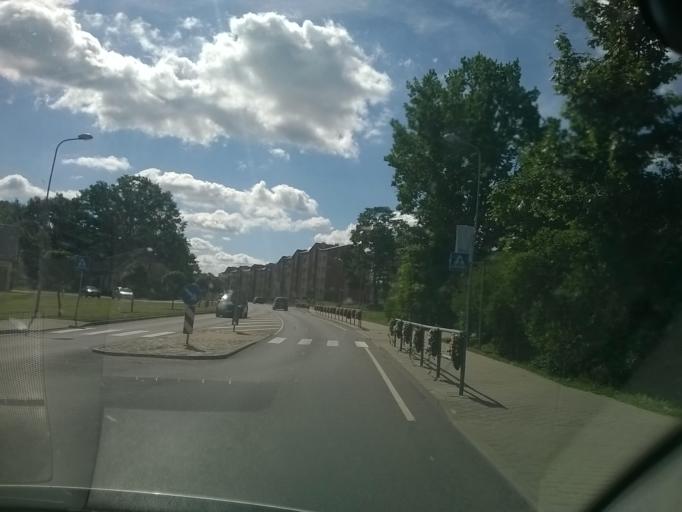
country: LV
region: Aluksnes Rajons
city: Aluksne
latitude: 57.4288
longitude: 27.0389
